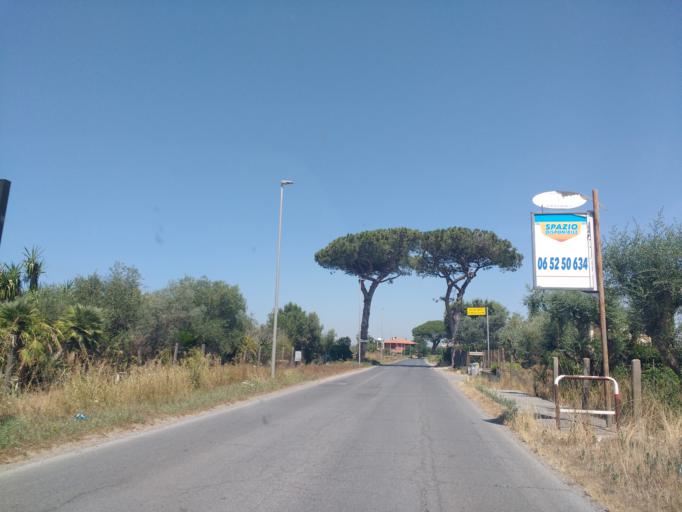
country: IT
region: Latium
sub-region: Citta metropolitana di Roma Capitale
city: Fregene
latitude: 41.8488
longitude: 12.2195
